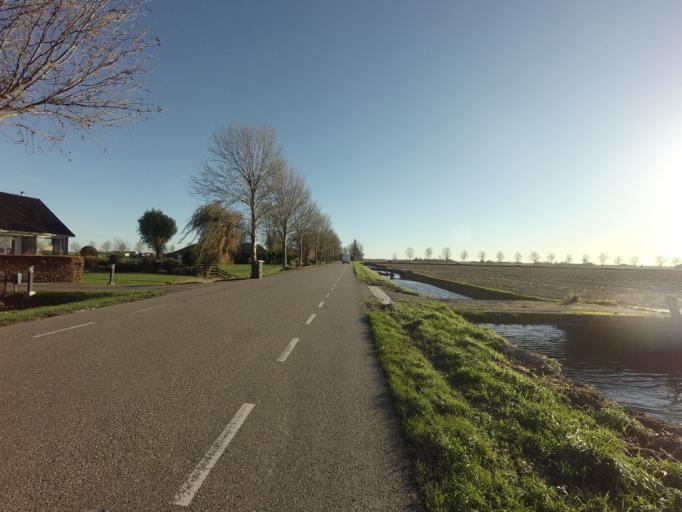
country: NL
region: South Holland
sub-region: Gemeente Nieuwkoop
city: Nieuwkoop
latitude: 52.1848
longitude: 4.7938
